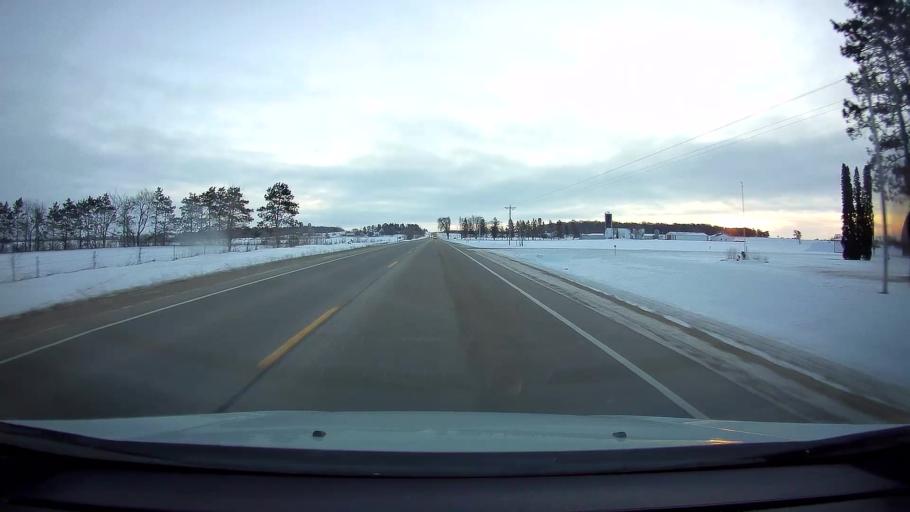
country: US
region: Wisconsin
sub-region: Saint Croix County
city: New Richmond
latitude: 45.1360
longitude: -92.4545
